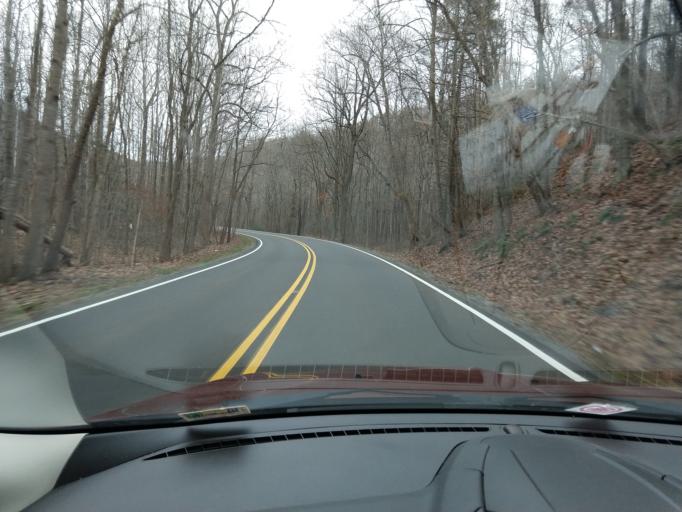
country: US
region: West Virginia
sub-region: Greenbrier County
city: White Sulphur Springs
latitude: 37.7252
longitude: -80.2199
